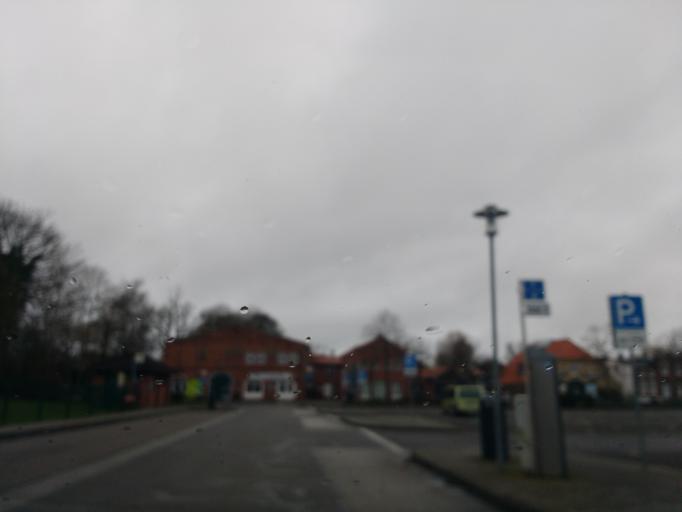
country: DE
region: Schleswig-Holstein
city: Burg auf Fehmarn
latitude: 54.4376
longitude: 11.2009
